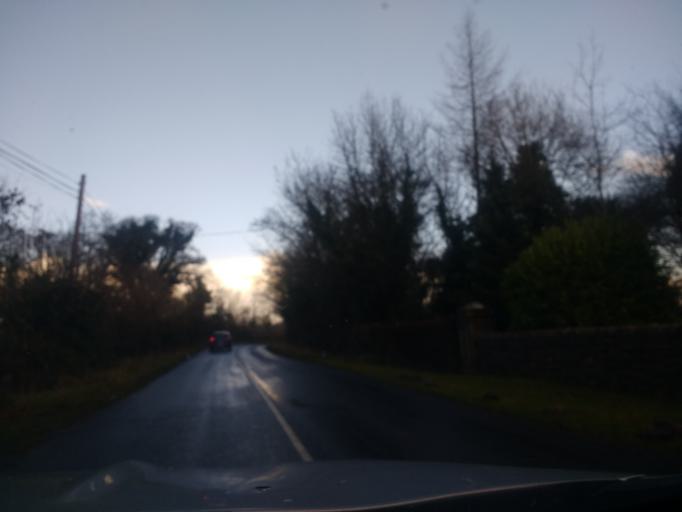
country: IE
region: Ulster
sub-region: County Donegal
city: Ramelton
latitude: 55.0472
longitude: -7.6430
